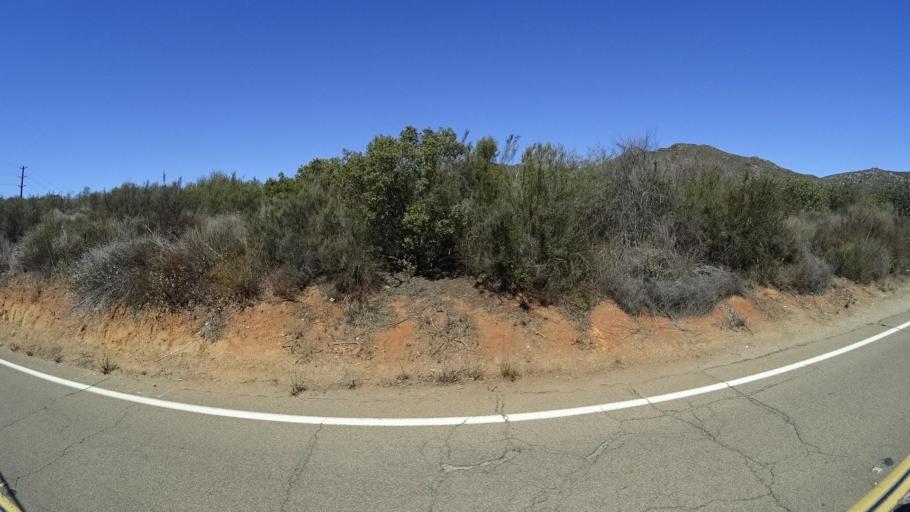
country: US
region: California
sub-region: San Diego County
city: Alpine
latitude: 32.7906
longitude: -116.7364
